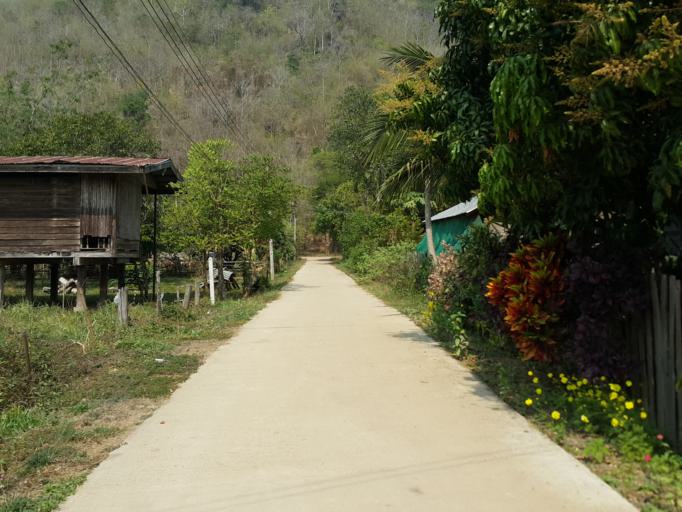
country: TH
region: Sukhothai
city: Thung Saliam
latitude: 17.3140
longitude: 99.5085
